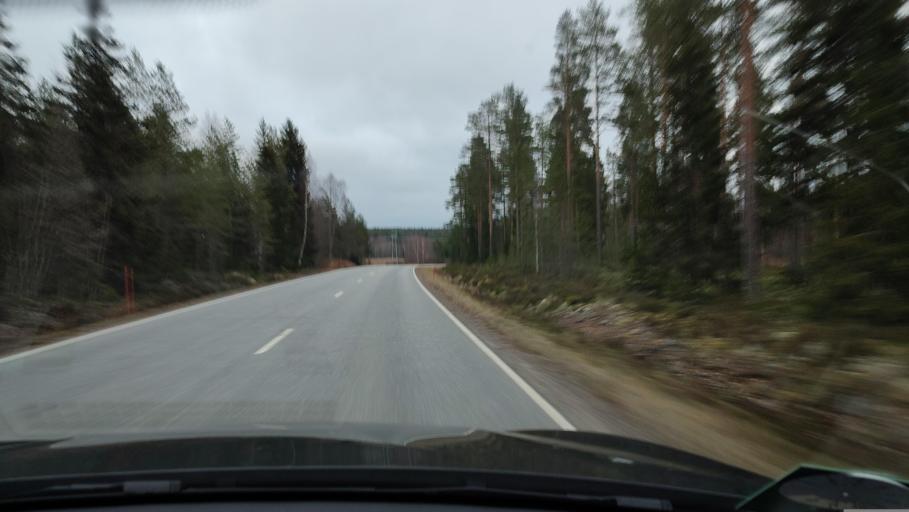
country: FI
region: Southern Ostrobothnia
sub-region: Suupohja
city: Karijoki
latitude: 62.2322
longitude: 21.7391
